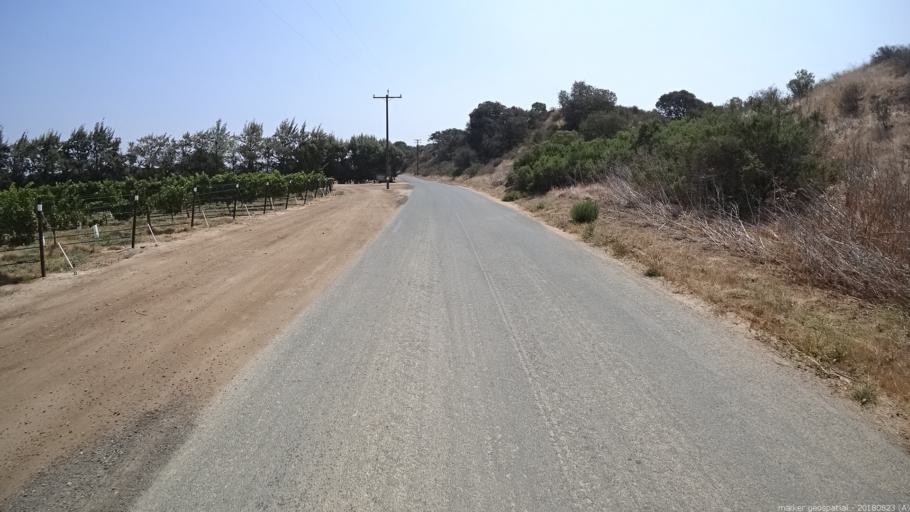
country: US
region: California
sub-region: Monterey County
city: Soledad
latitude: 36.3671
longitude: -121.3129
